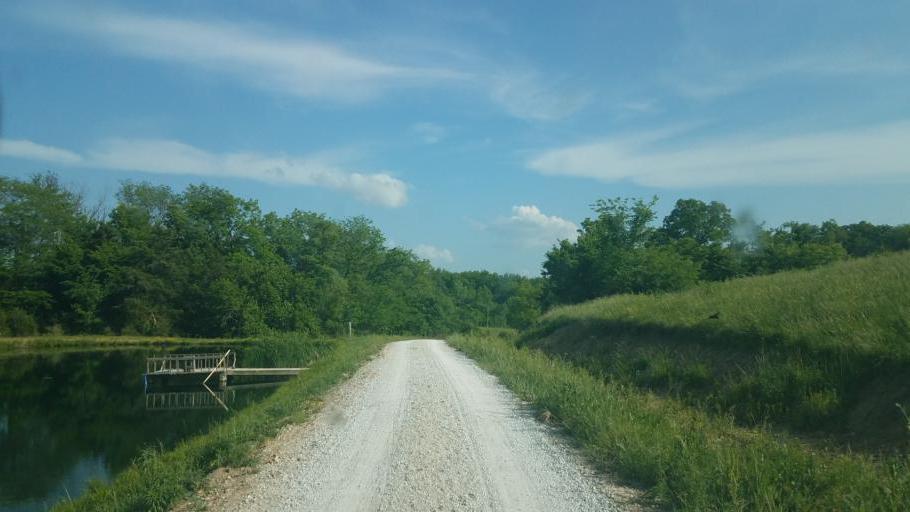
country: US
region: Missouri
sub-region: Cooper County
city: Boonville
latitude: 38.8529
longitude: -92.6458
